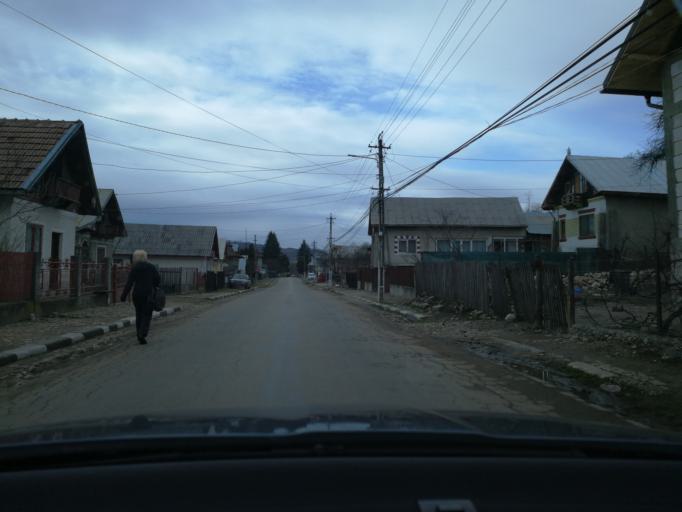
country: RO
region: Dambovita
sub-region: Comuna Buciumeni
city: Valea Leurzii
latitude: 45.1395
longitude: 25.4872
